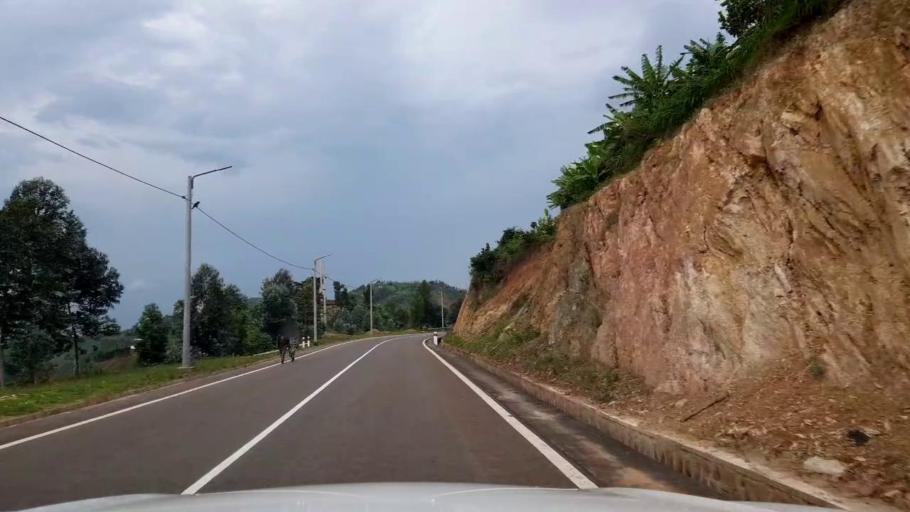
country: RW
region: Western Province
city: Kibuye
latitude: -2.0246
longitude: 29.3886
